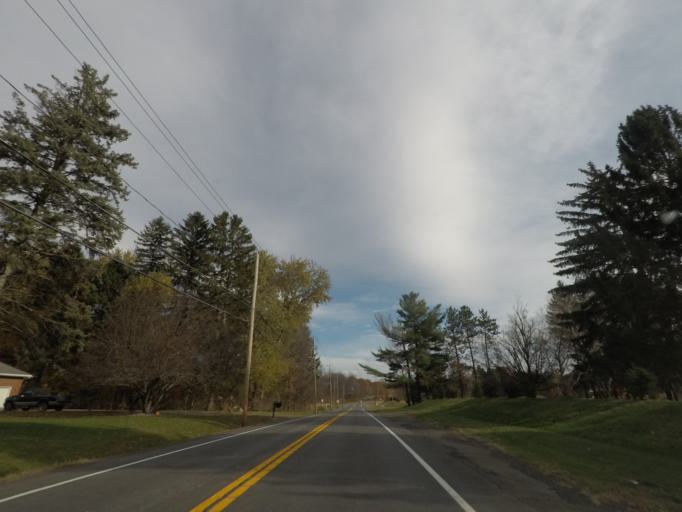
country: US
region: New York
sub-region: Albany County
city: Voorheesville
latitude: 42.6446
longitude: -73.9077
